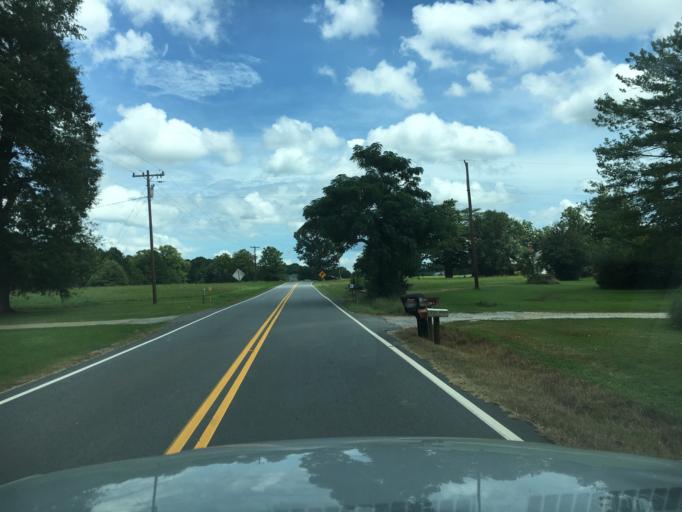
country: US
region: South Carolina
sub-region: Anderson County
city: Belton
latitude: 34.5391
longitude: -82.4436
